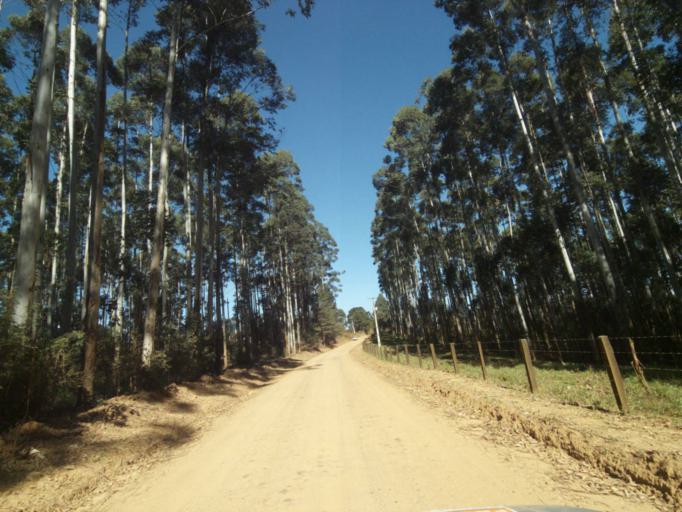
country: BR
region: Parana
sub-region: Tibagi
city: Tibagi
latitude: -24.5537
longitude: -50.6214
